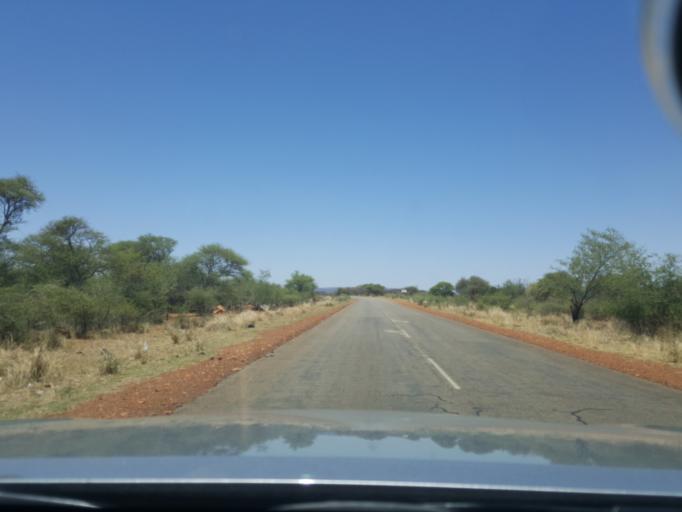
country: BW
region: South East
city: Otse
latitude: -25.1164
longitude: 25.9472
